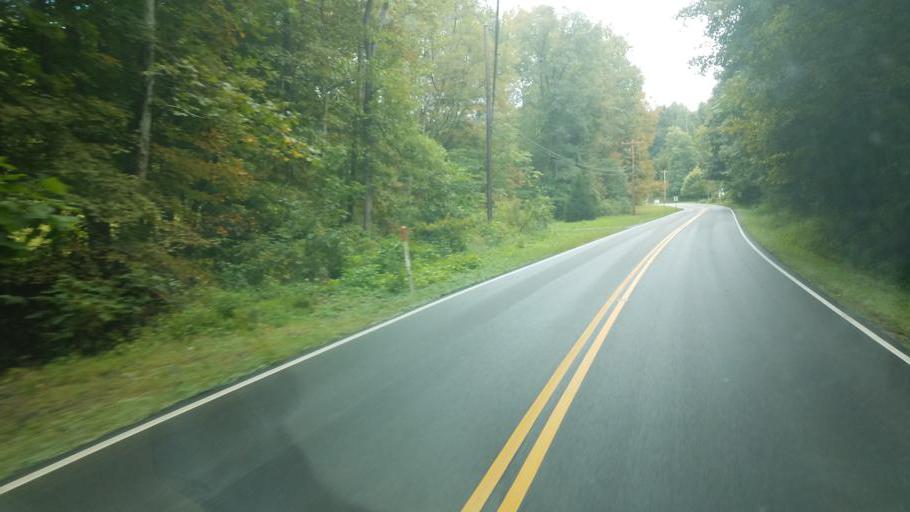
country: US
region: Ohio
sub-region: Scioto County
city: Lucasville
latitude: 38.8642
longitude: -82.9355
